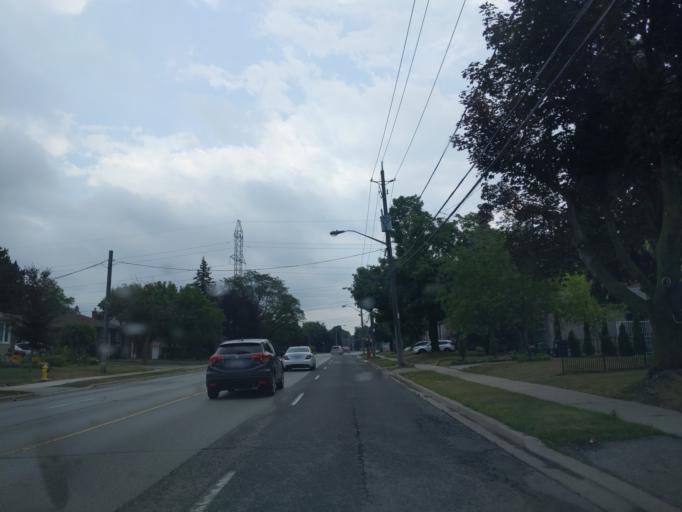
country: CA
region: Ontario
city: North York
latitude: 43.7855
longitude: -79.4090
